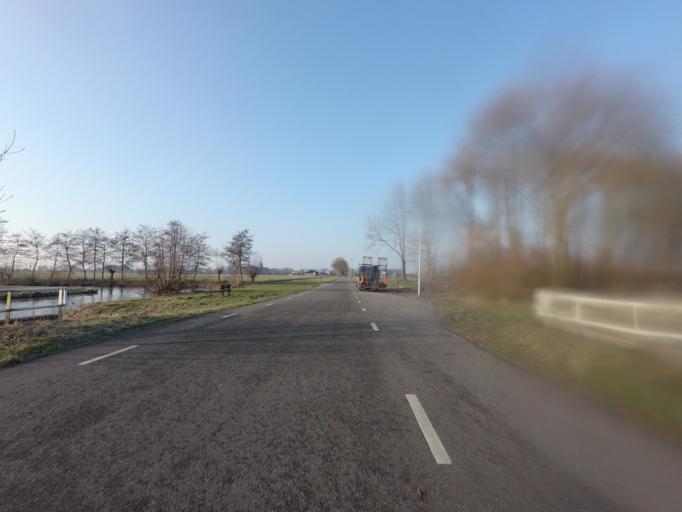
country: NL
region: South Holland
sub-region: Gemeente Vlist
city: Vlist
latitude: 52.0073
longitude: 4.8108
